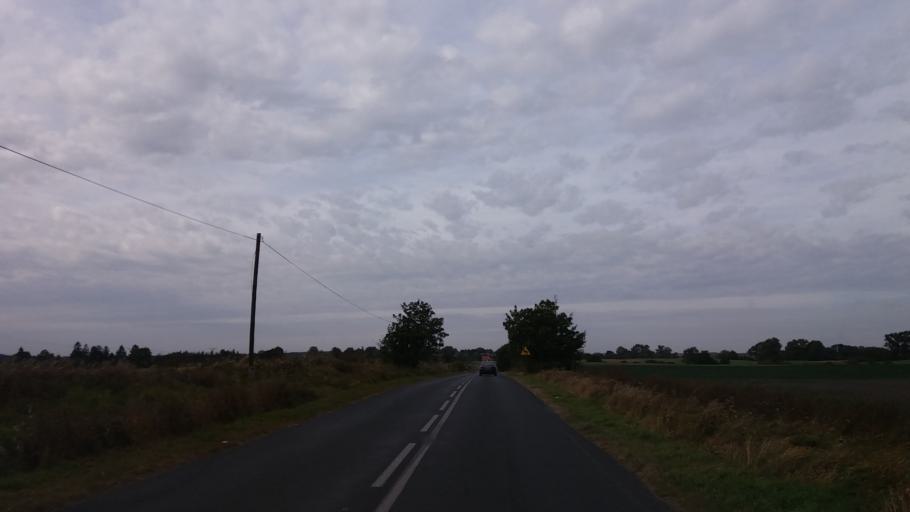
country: PL
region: Lubusz
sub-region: Powiat strzelecko-drezdenecki
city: Strzelce Krajenskie
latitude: 52.9162
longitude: 15.4930
